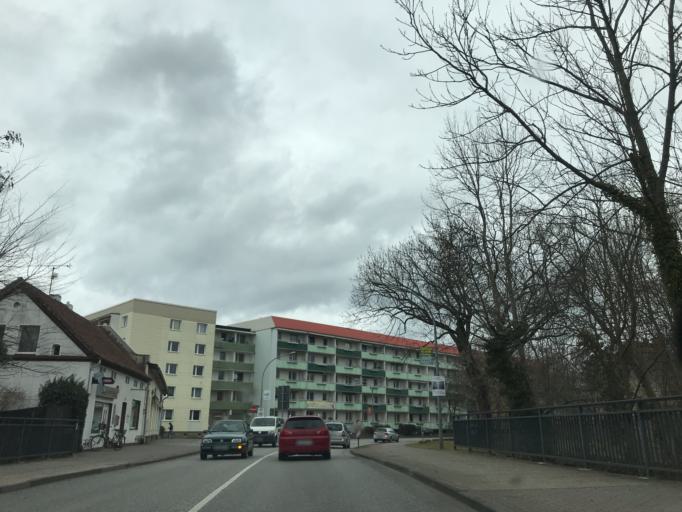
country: DE
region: Brandenburg
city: Luebben
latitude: 51.9387
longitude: 13.8907
